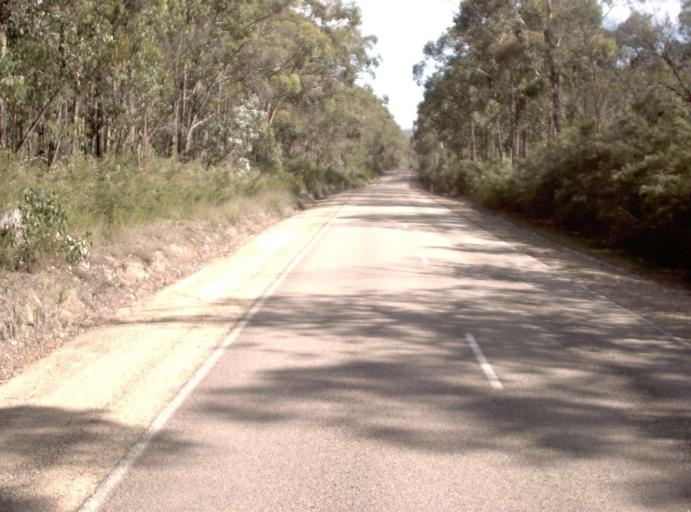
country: AU
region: Victoria
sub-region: East Gippsland
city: Lakes Entrance
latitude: -37.6355
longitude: 148.1105
